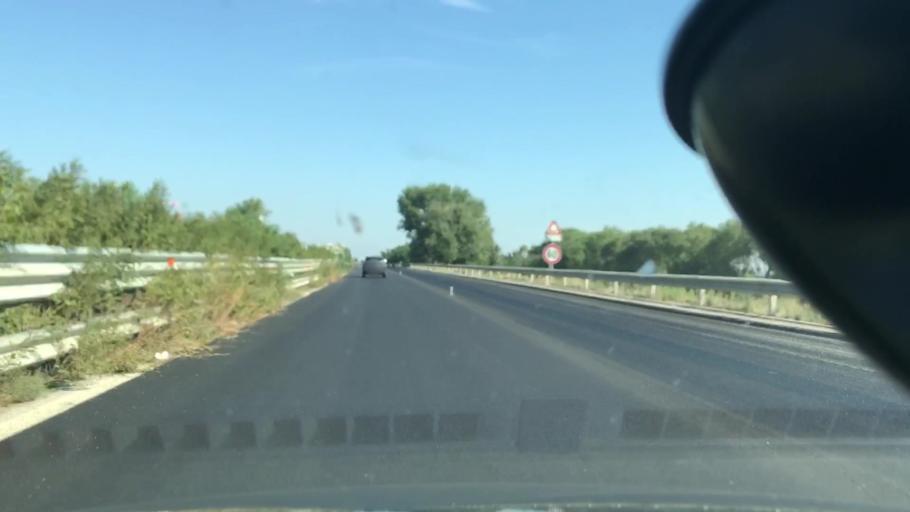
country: IT
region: Apulia
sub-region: Provincia di Foggia
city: Ascoli Satriano
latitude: 41.2729
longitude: 15.5530
